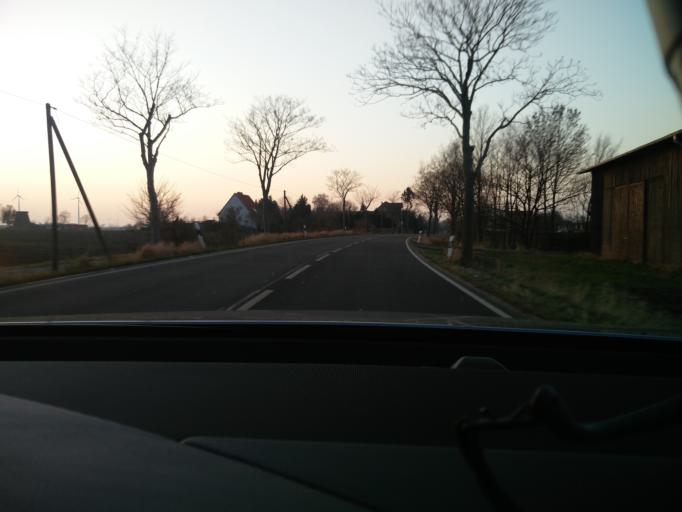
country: DE
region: Lower Saxony
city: Hohenhameln
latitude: 52.3022
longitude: 10.1032
